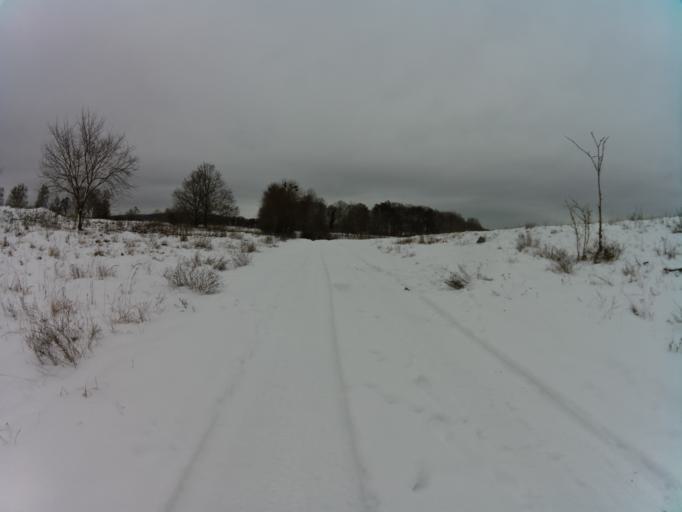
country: PL
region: West Pomeranian Voivodeship
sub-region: Powiat choszczenski
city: Recz
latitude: 53.3394
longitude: 15.5401
